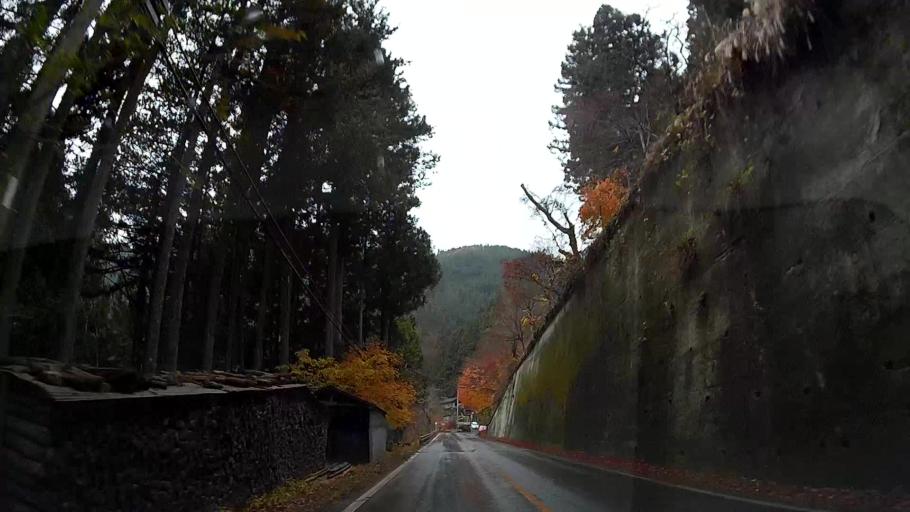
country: JP
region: Saitama
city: Chichibu
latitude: 35.9487
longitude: 138.9164
